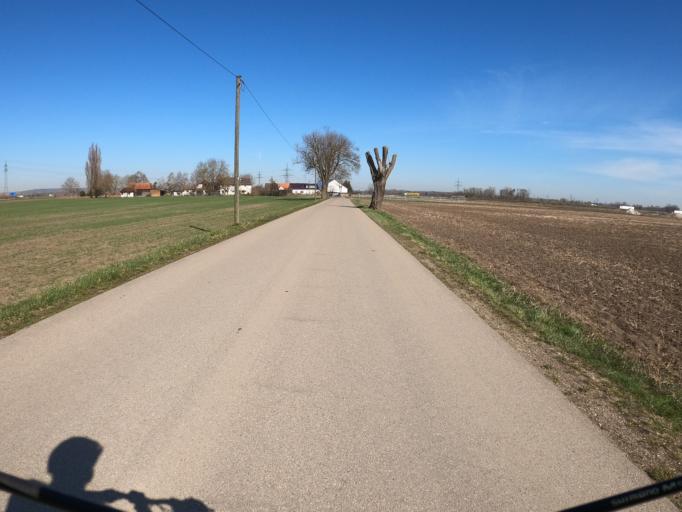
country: DE
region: Bavaria
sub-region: Swabia
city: Nersingen
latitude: 48.4577
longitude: 10.1485
